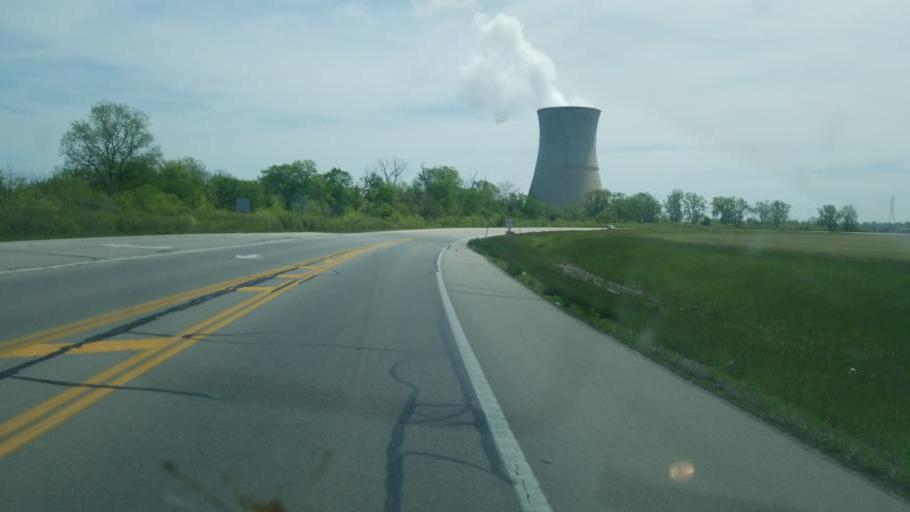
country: US
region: Ohio
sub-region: Ottawa County
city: Oak Harbor
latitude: 41.6034
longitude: -83.1012
